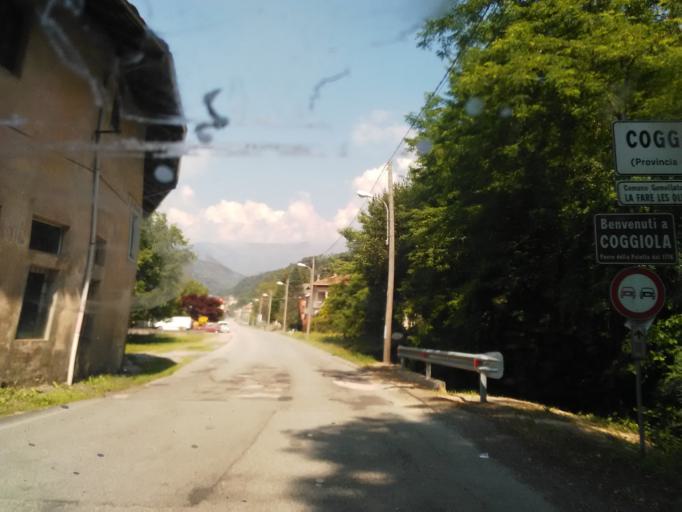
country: IT
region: Piedmont
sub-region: Provincia di Biella
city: Pray
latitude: 45.6804
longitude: 8.1982
